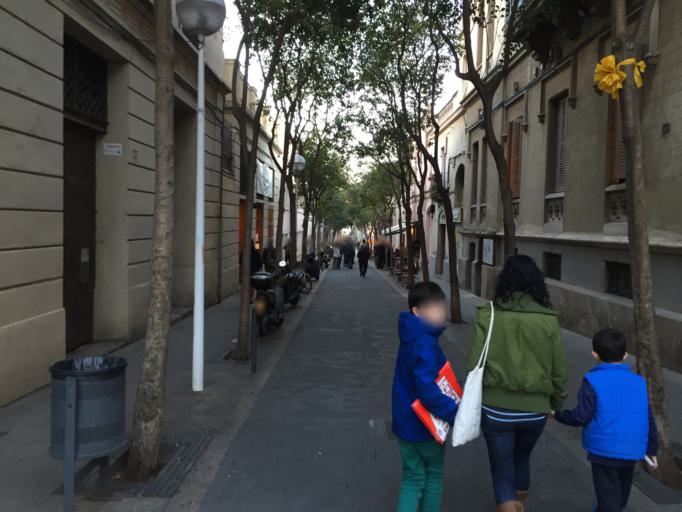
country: ES
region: Catalonia
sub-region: Provincia de Barcelona
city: Gracia
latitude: 41.4048
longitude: 2.1575
